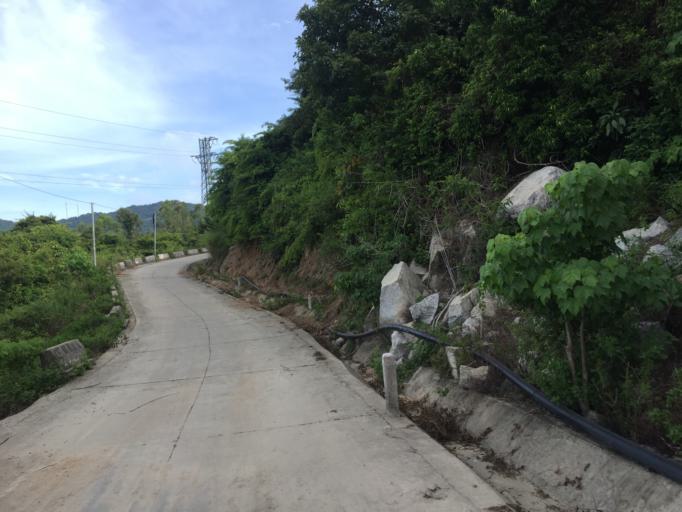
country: VN
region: Quang Nam
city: Hoi An
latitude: 15.9546
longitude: 108.5090
